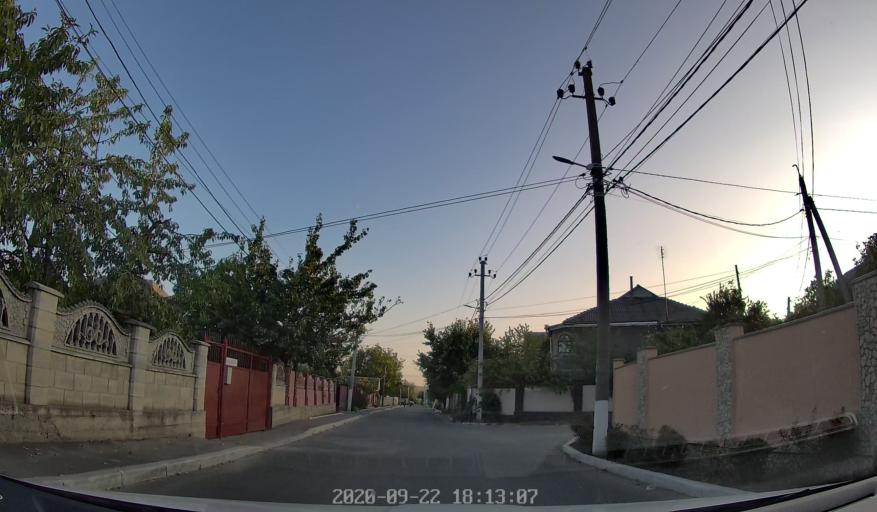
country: MD
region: Laloveni
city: Ialoveni
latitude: 46.9455
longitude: 28.7896
